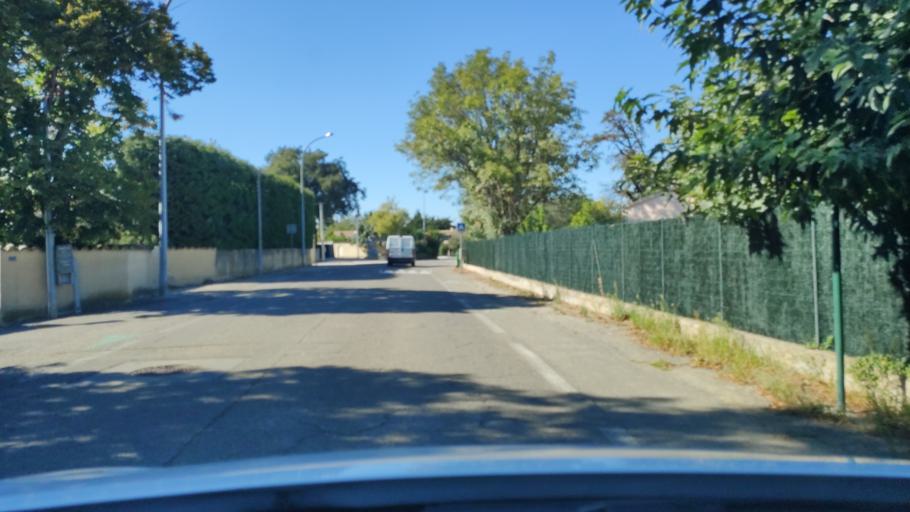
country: FR
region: Provence-Alpes-Cote d'Azur
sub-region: Departement du Vaucluse
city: Morieres-les-Avignon
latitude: 43.9454
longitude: 4.8977
